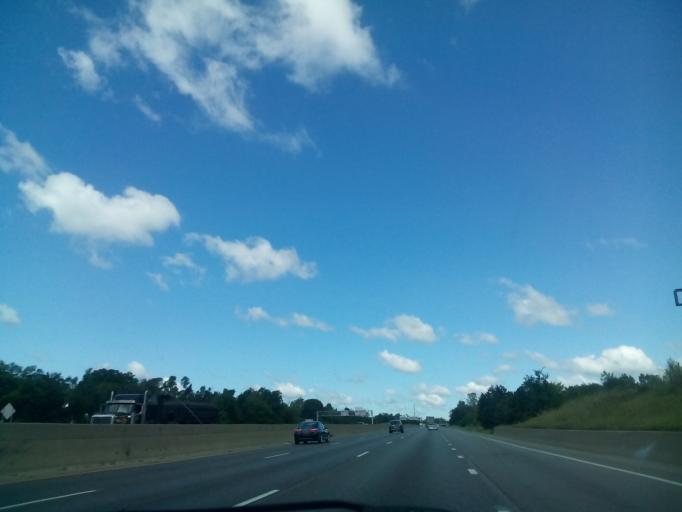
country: US
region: Michigan
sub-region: Genesee County
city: Flint
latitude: 42.9913
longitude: -83.7409
